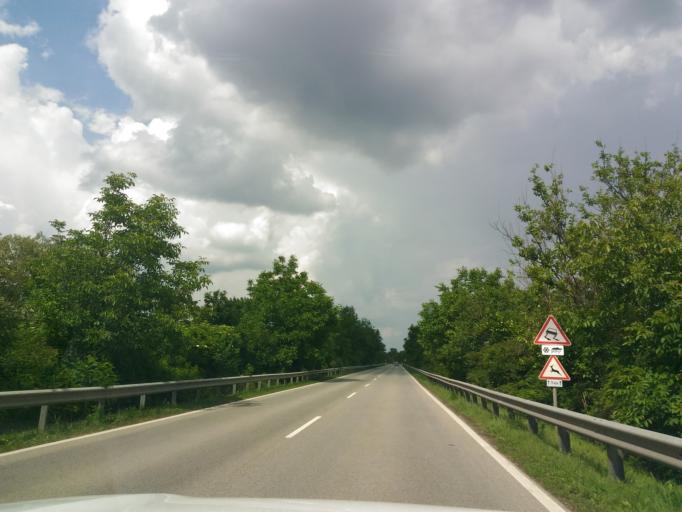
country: HU
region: Baranya
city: Hidas
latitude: 46.2708
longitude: 18.5138
